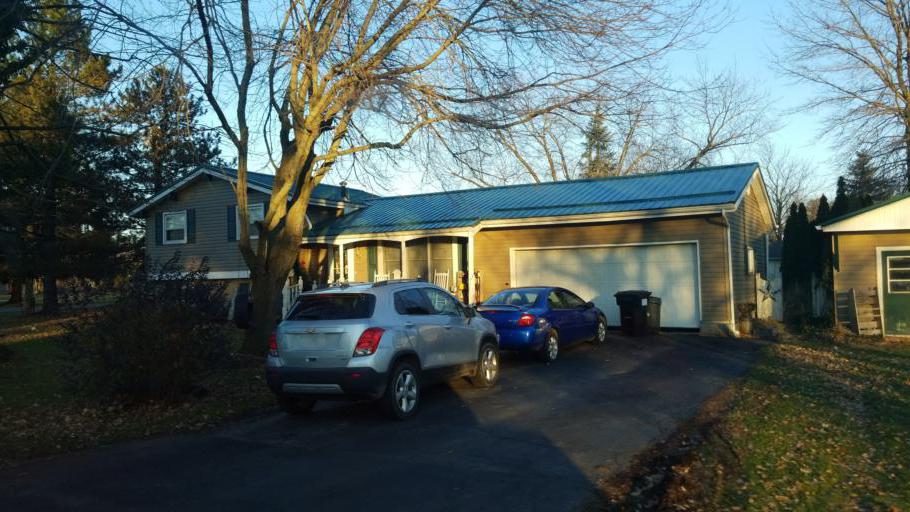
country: US
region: Ohio
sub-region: Wyandot County
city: Upper Sandusky
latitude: 40.8222
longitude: -83.1338
